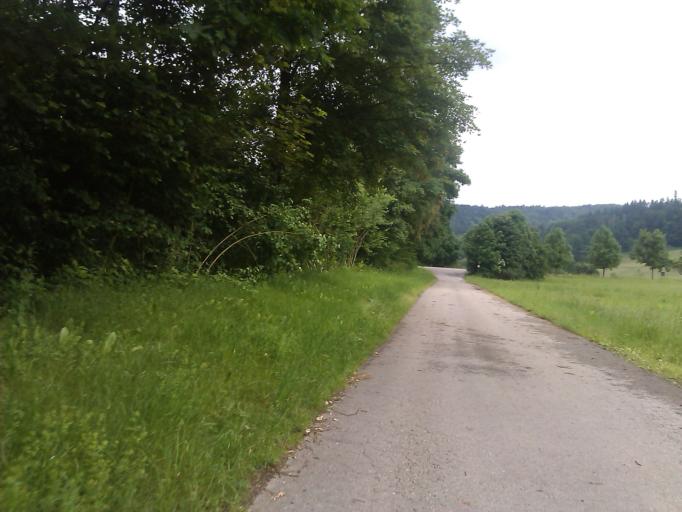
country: DE
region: Baden-Wuerttemberg
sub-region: Regierungsbezirk Stuttgart
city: Gaildorf
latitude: 48.9683
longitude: 9.8210
